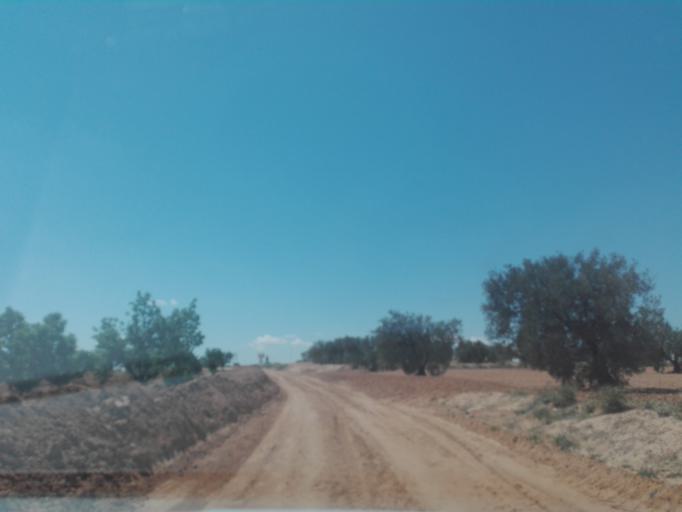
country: TN
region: Safaqis
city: Bi'r `Ali Bin Khalifah
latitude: 34.7900
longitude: 10.3376
